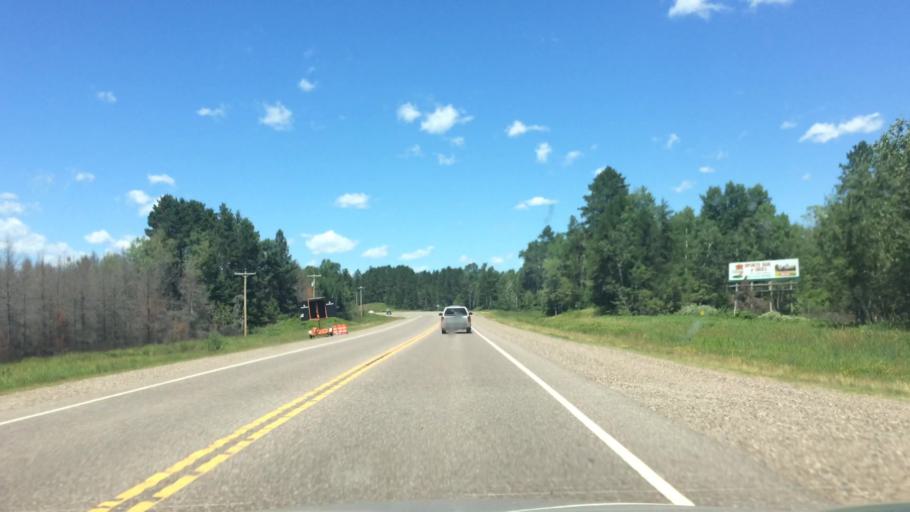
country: US
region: Wisconsin
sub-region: Lincoln County
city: Tomahawk
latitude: 45.6529
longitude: -89.7049
